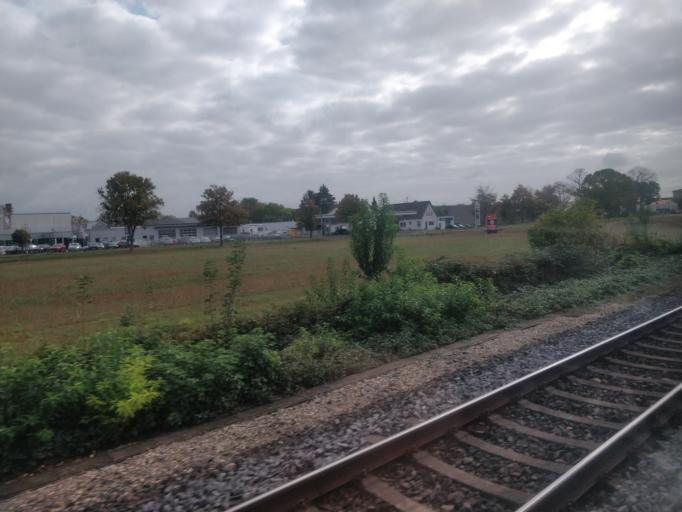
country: DE
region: North Rhine-Westphalia
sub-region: Regierungsbezirk Koln
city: Wahn-Heide
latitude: 50.8392
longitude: 7.0995
